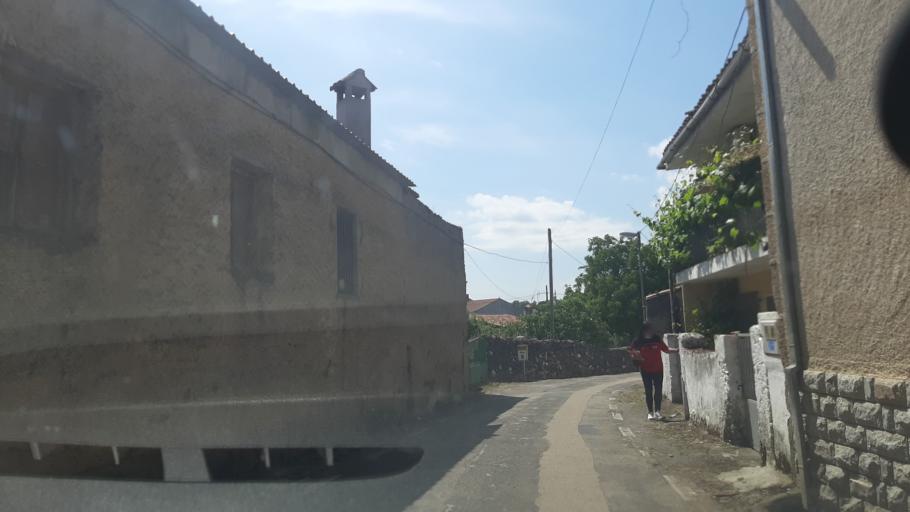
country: ES
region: Castille and Leon
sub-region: Provincia de Salamanca
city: Gallegos de Arganan
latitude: 40.6504
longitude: -6.7574
